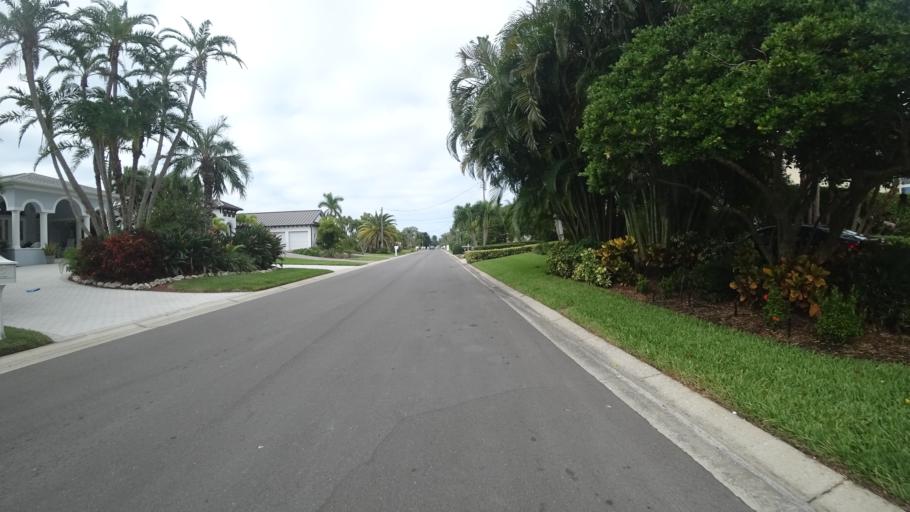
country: US
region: Florida
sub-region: Manatee County
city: Longboat Key
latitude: 27.4218
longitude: -82.6622
